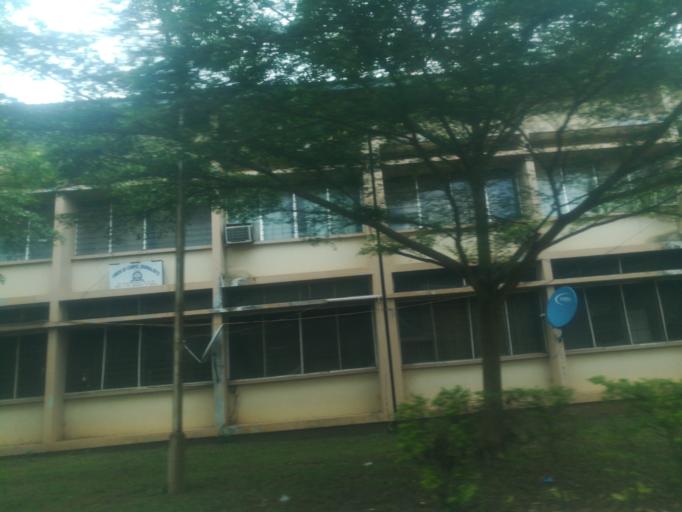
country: NG
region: Oyo
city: Ibadan
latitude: 7.4451
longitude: 3.8985
